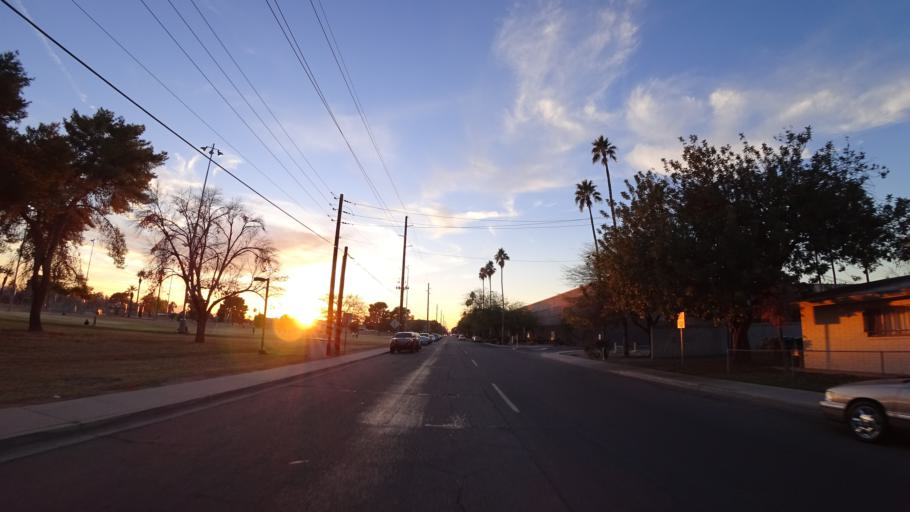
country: US
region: Arizona
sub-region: Maricopa County
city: Tempe Junction
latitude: 33.4729
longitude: -111.9830
